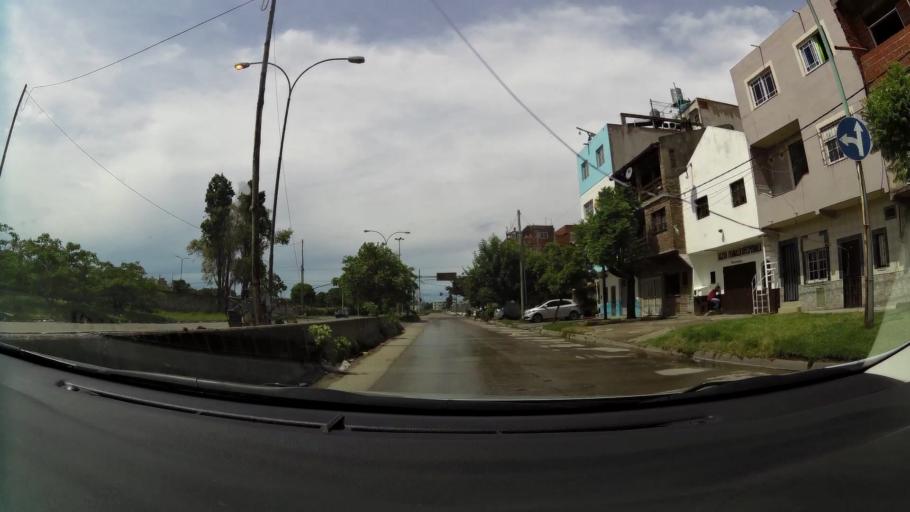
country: AR
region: Buenos Aires F.D.
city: Villa Lugano
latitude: -34.6546
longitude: -58.4576
